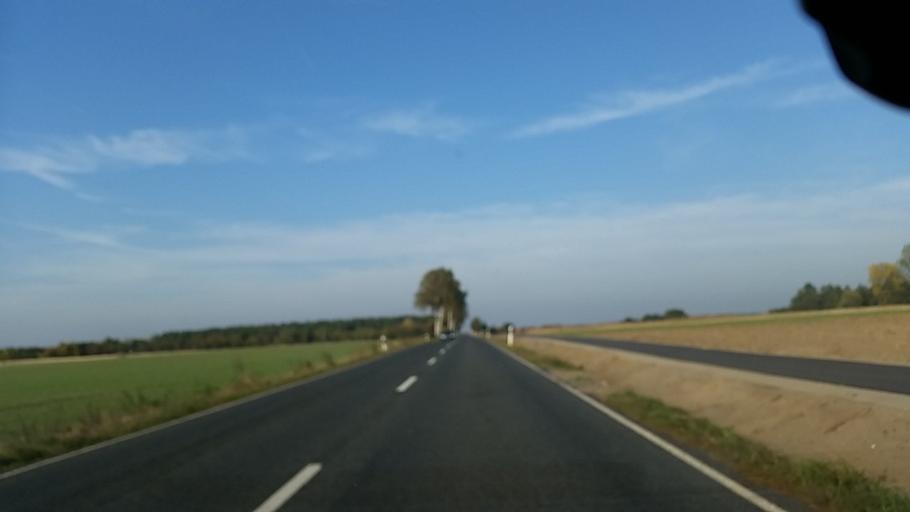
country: DE
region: Lower Saxony
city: Gross Twulpstedt
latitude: 52.3787
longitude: 10.8504
